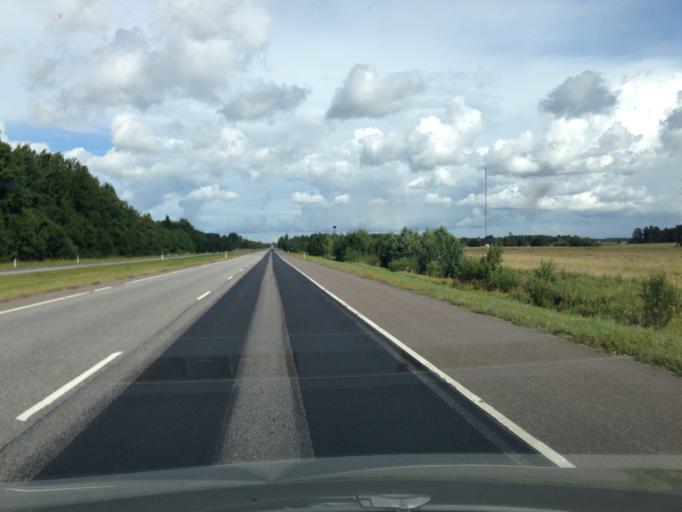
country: EE
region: Harju
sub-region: Saue linn
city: Saue
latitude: 59.2806
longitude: 24.5292
